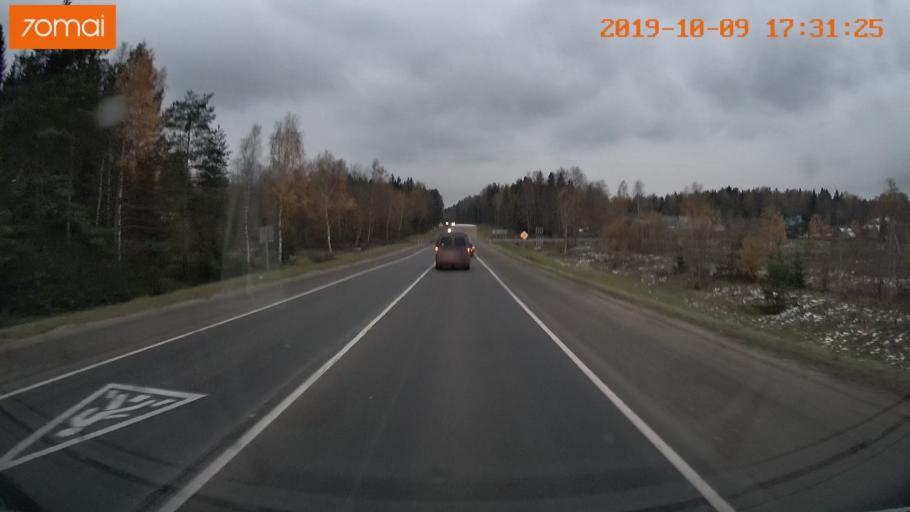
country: RU
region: Ivanovo
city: Bogorodskoye
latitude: 57.1357
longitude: 41.0395
